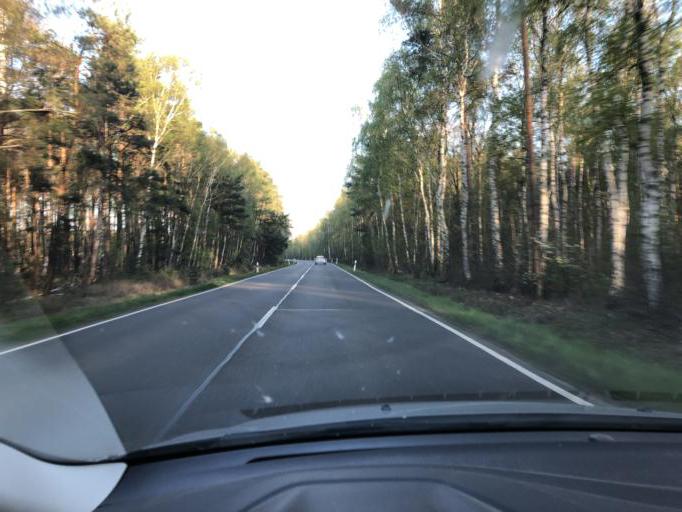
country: DE
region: Brandenburg
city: Welzow
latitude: 51.5481
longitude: 14.1578
